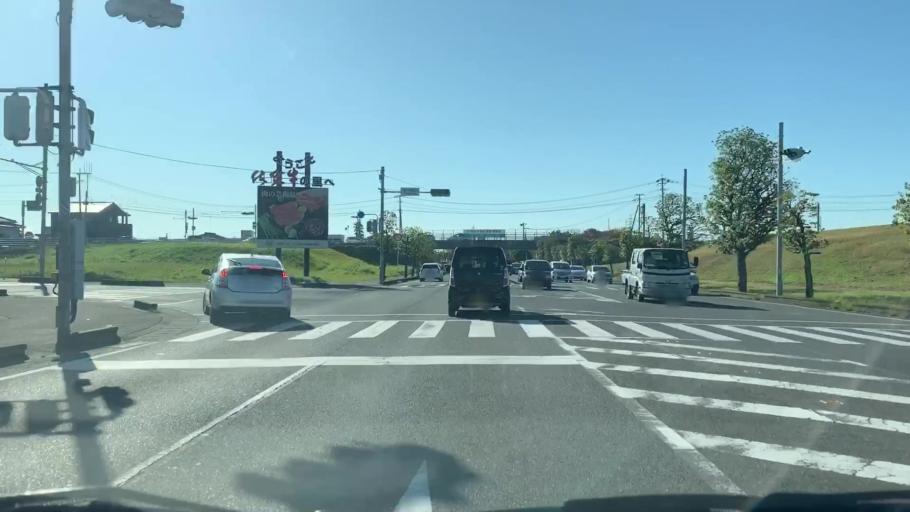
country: JP
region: Saga Prefecture
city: Saga-shi
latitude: 33.3106
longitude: 130.2763
